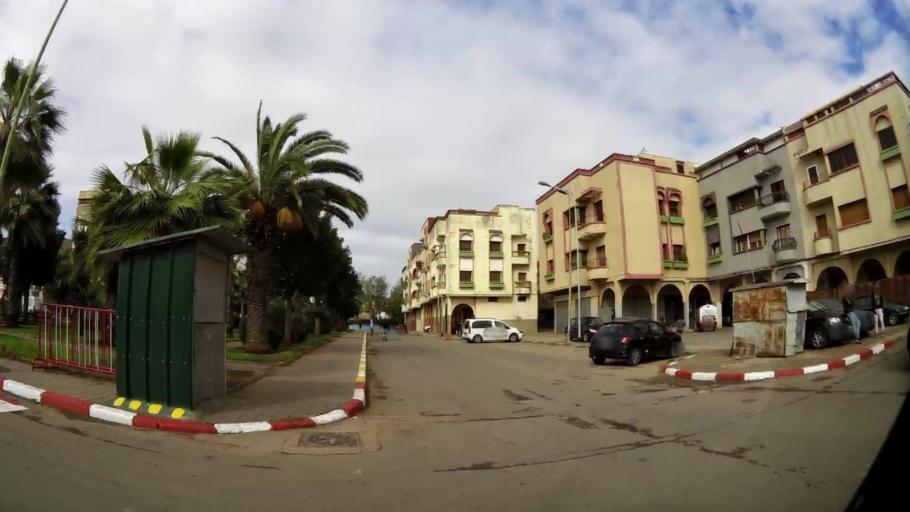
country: MA
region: Grand Casablanca
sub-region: Mohammedia
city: Mohammedia
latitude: 33.6840
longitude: -7.3754
